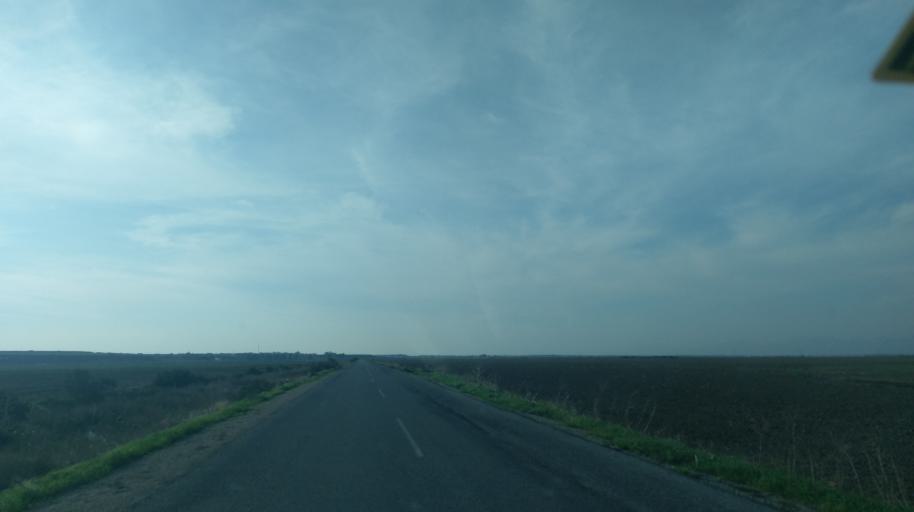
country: CY
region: Ammochostos
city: Acheritou
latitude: 35.0950
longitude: 33.8315
